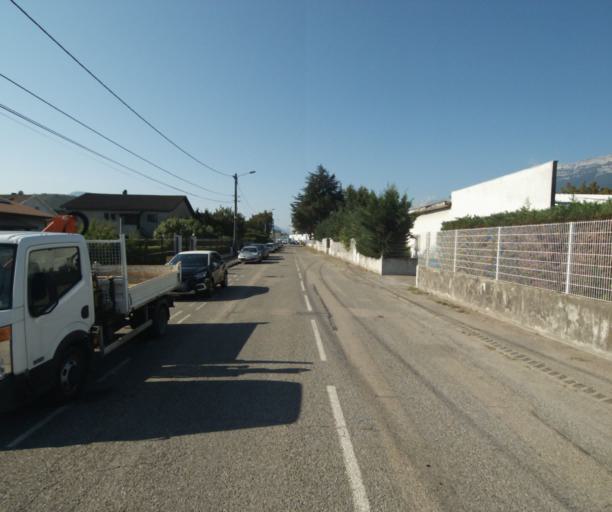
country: FR
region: Rhone-Alpes
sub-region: Departement de l'Isere
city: Echirolles
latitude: 45.1424
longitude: 5.7110
